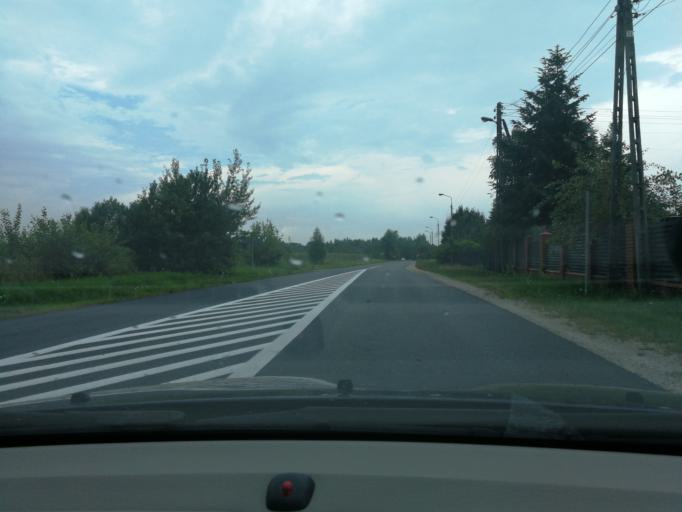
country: PL
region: Masovian Voivodeship
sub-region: Powiat zyrardowski
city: Radziejowice
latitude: 52.0091
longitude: 20.5586
